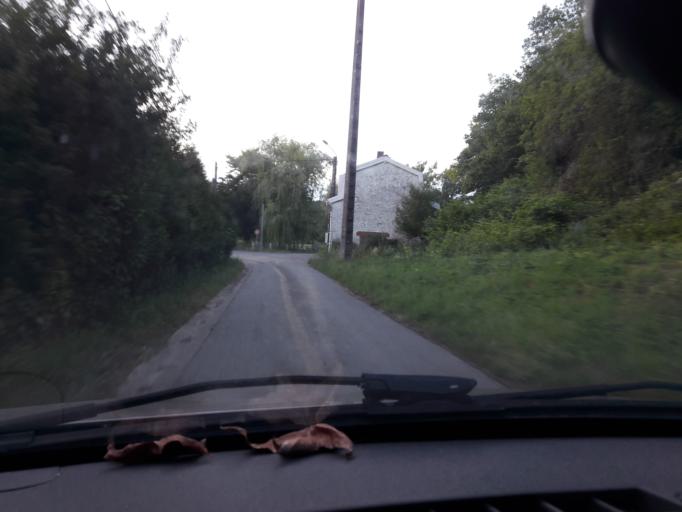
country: BE
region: Wallonia
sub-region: Province du Hainaut
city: Merbes-le-Chateau
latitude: 50.2640
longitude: 4.1811
